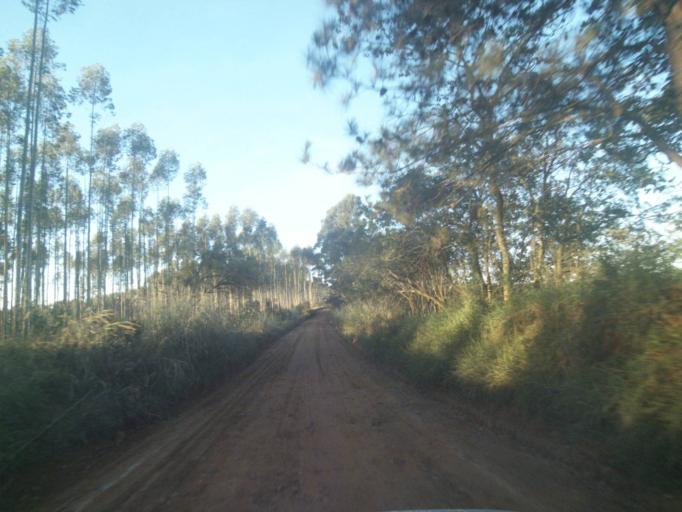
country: BR
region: Parana
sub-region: Tibagi
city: Tibagi
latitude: -24.5566
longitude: -50.5744
